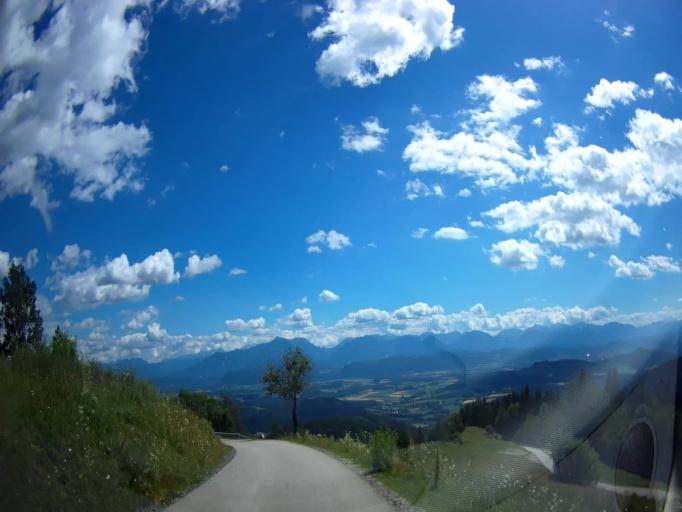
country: AT
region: Carinthia
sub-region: Politischer Bezirk Sankt Veit an der Glan
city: St. Georgen am Laengsee
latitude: 46.7269
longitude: 14.4282
